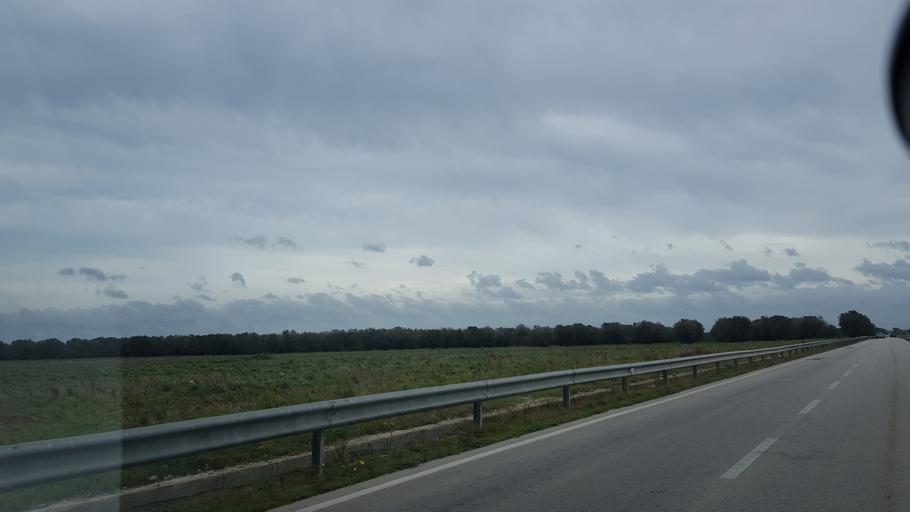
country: IT
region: Apulia
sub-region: Provincia di Brindisi
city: San Pancrazio Salentino
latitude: 40.4088
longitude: 17.8781
